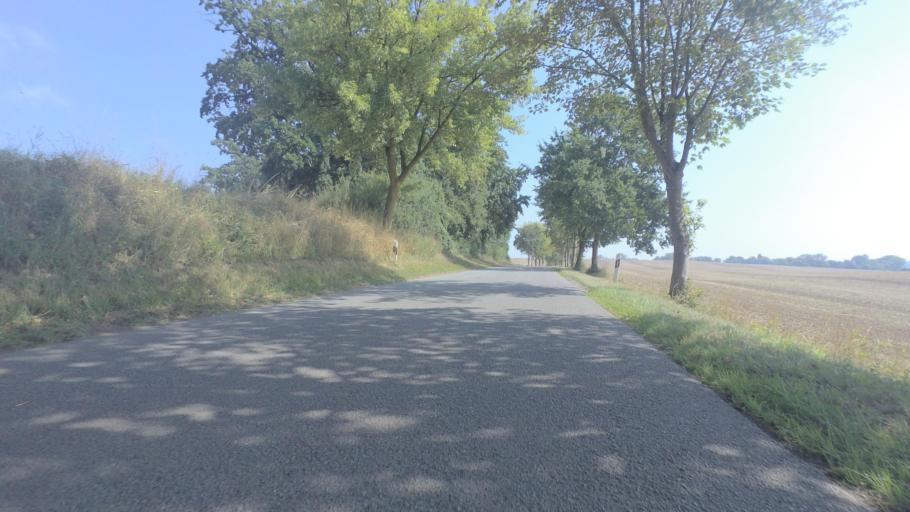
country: DE
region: Mecklenburg-Vorpommern
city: Pampow
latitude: 53.6870
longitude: 12.5864
